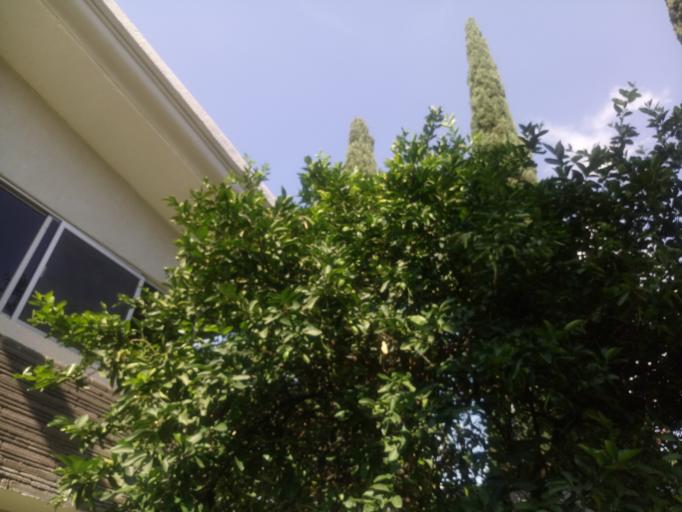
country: MX
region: Puebla
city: Puebla
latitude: 19.0164
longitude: -98.2167
